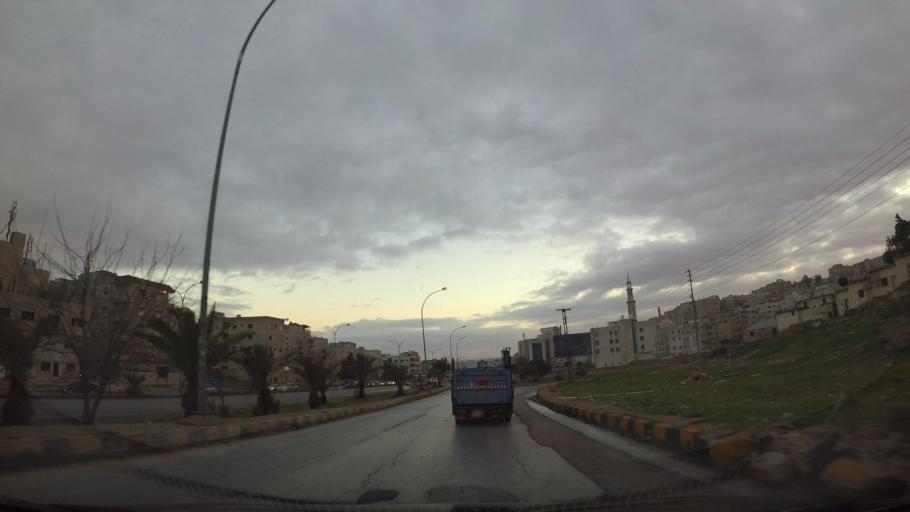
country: JO
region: Amman
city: Amman
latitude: 31.9913
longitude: 35.9177
